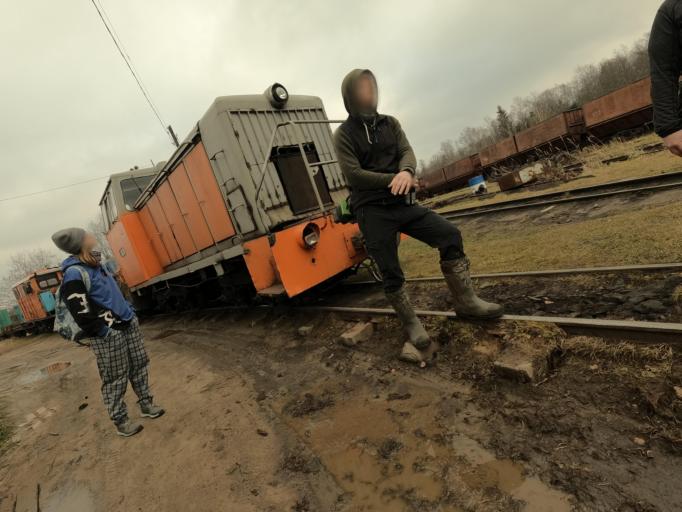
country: RU
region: Leningrad
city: Nurma
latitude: 59.6016
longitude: 31.2004
